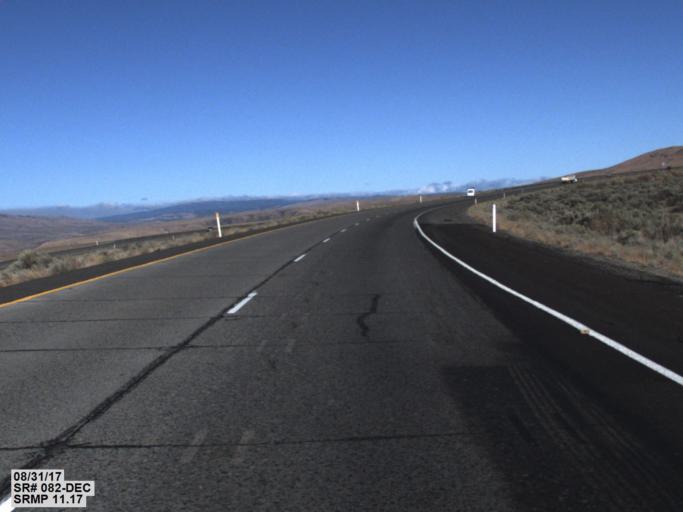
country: US
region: Washington
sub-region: Kittitas County
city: Kittitas
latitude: 46.8475
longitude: -120.3856
